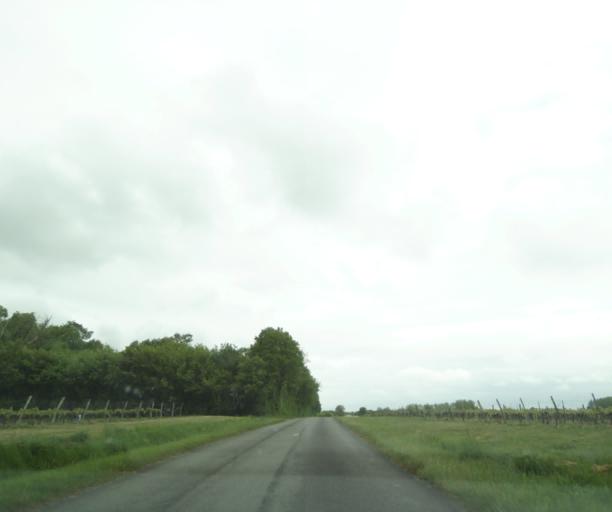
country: FR
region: Poitou-Charentes
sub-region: Departement de la Charente-Maritime
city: Chaniers
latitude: 45.6898
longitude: -0.5010
